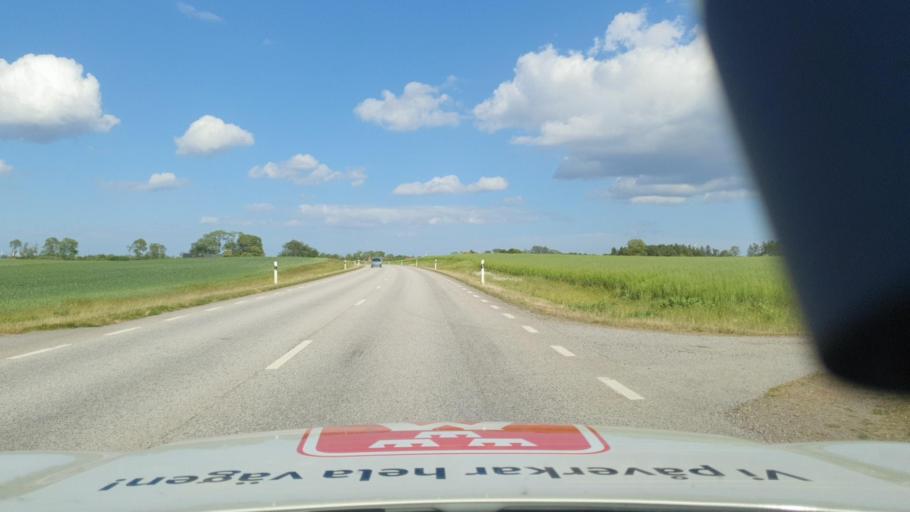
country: SE
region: Skane
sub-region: Simrishamns Kommun
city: Simrishamn
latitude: 55.5353
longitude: 14.3036
